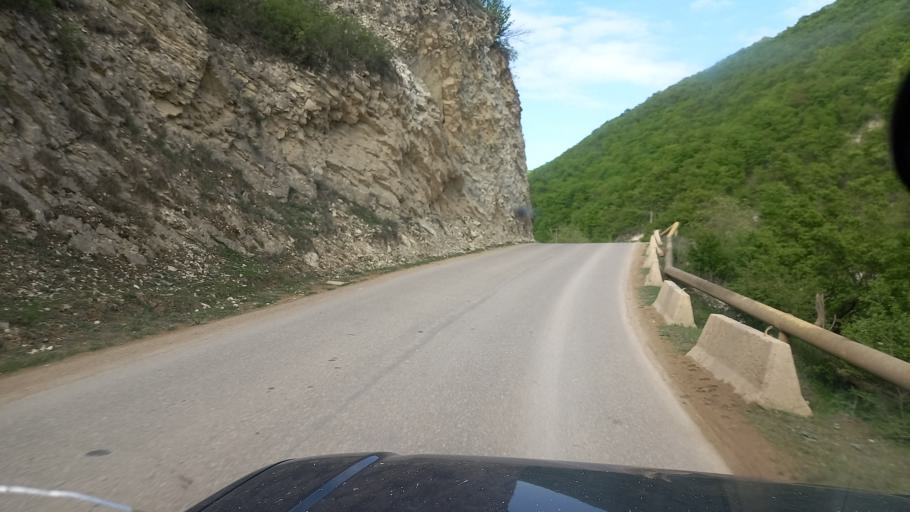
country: RU
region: Dagestan
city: Khuchni
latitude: 41.9640
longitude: 47.9581
